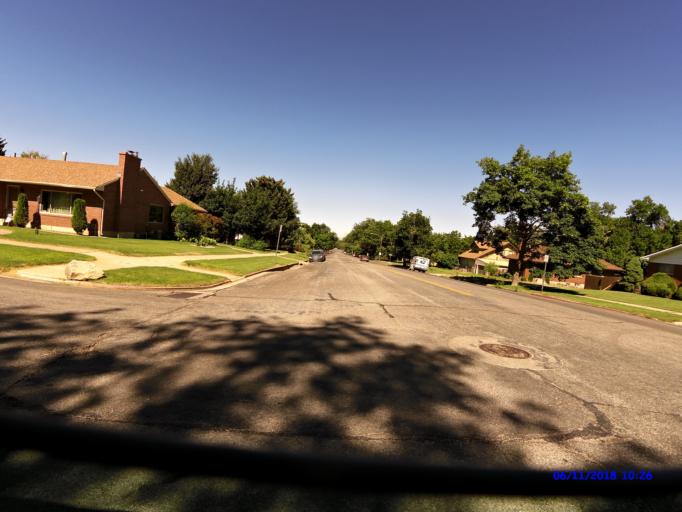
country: US
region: Utah
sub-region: Weber County
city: Ogden
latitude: 41.2202
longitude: -111.9427
